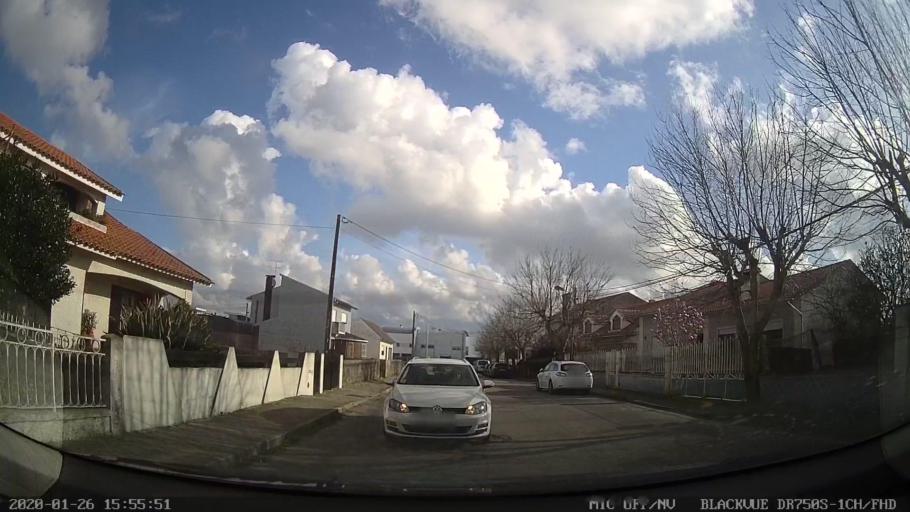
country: PT
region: Aveiro
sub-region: Aveiro
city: Aradas
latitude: 40.6300
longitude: -8.6290
